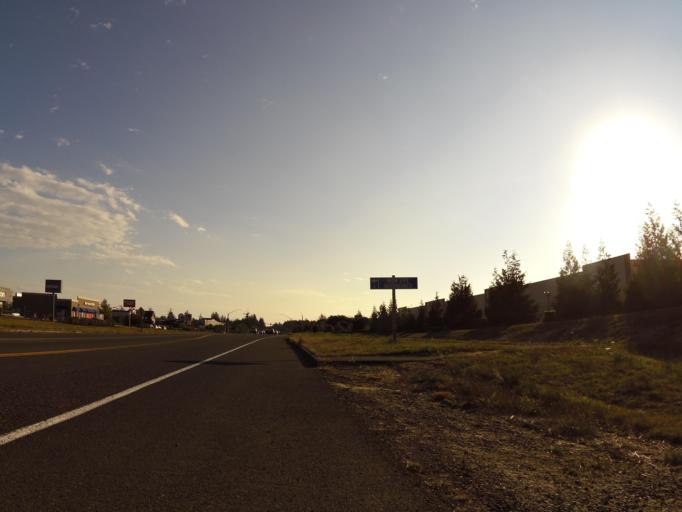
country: US
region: Oregon
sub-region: Clatsop County
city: Warrenton
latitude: 46.1494
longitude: -123.9160
